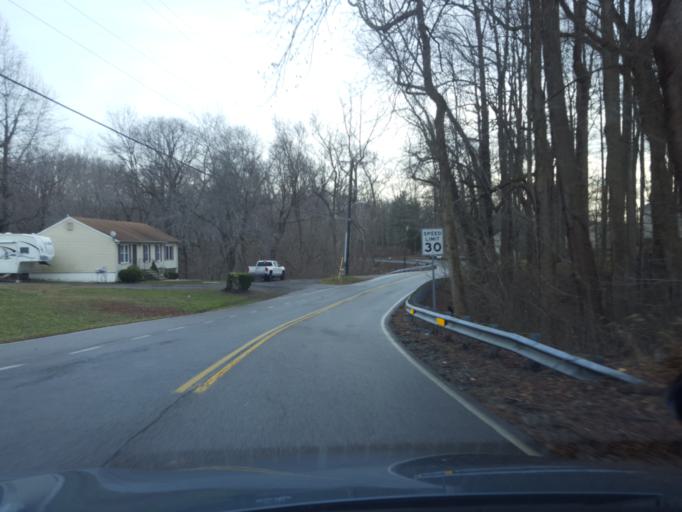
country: US
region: Maryland
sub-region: Calvert County
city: Chesapeake Beach
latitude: 38.6786
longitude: -76.5486
